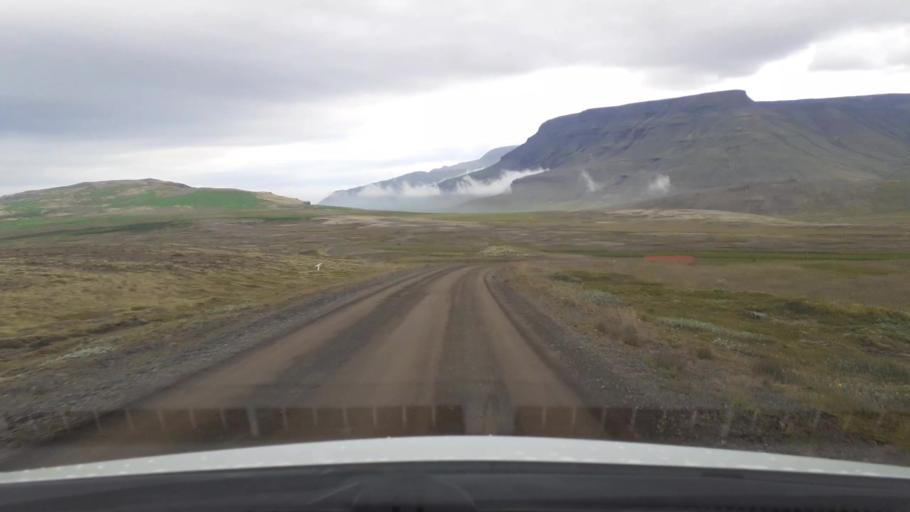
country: IS
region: Capital Region
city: Mosfellsbaer
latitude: 64.1971
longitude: -21.5536
